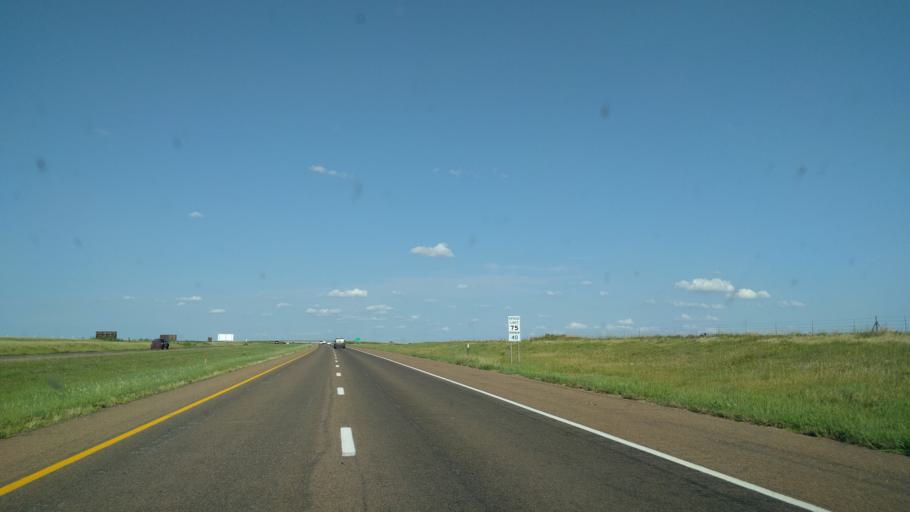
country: US
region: Kansas
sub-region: Ellis County
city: Ellis
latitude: 38.9494
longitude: -99.5500
